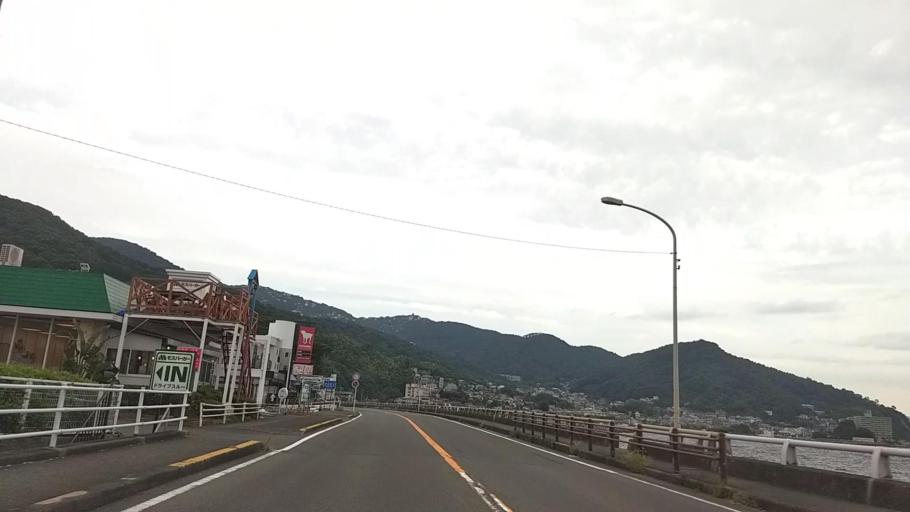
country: JP
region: Shizuoka
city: Atami
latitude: 35.0506
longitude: 139.0711
